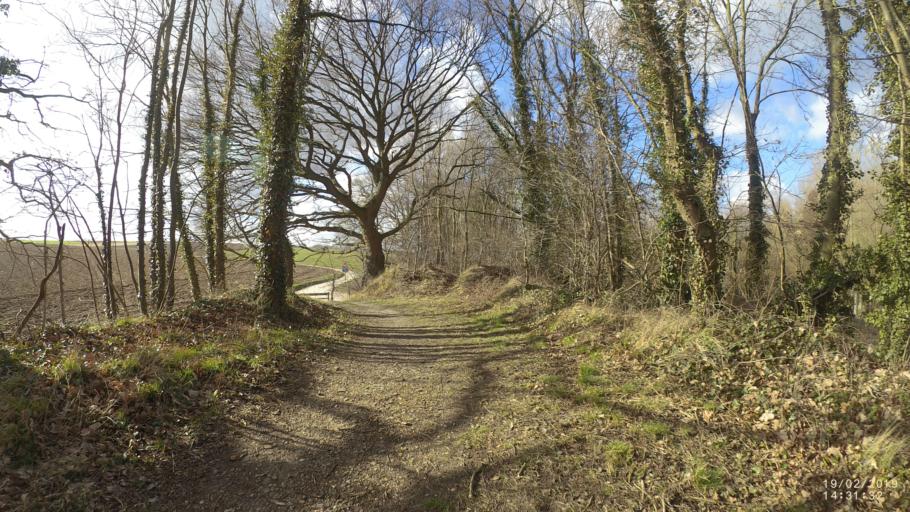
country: BE
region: Flanders
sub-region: Provincie Limburg
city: Tongeren
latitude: 50.7920
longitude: 5.4395
